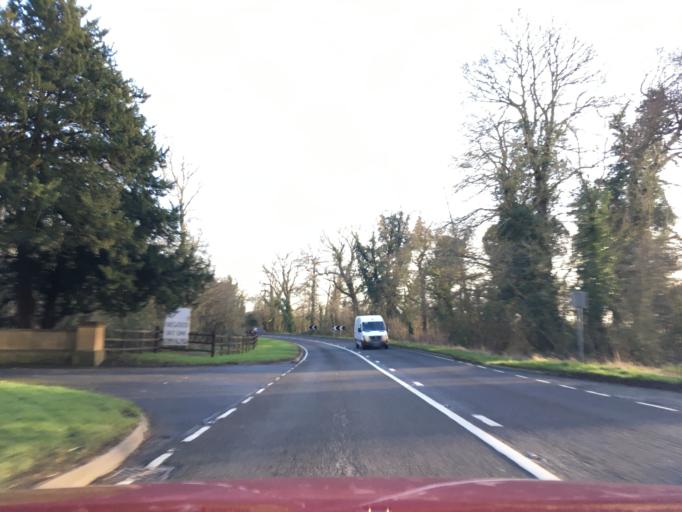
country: GB
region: England
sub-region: Warwickshire
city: Henley in Arden
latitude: 52.2504
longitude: -1.7564
